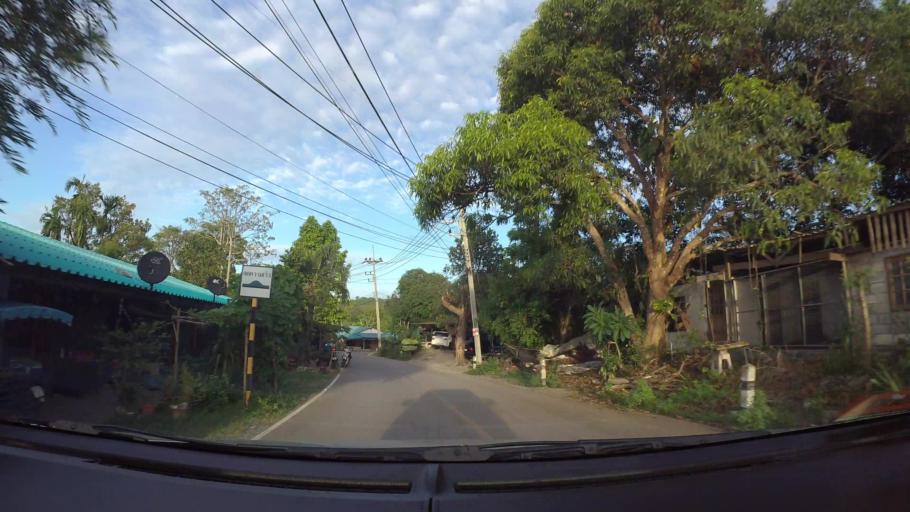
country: TH
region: Chon Buri
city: Sattahip
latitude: 12.7480
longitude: 100.9343
